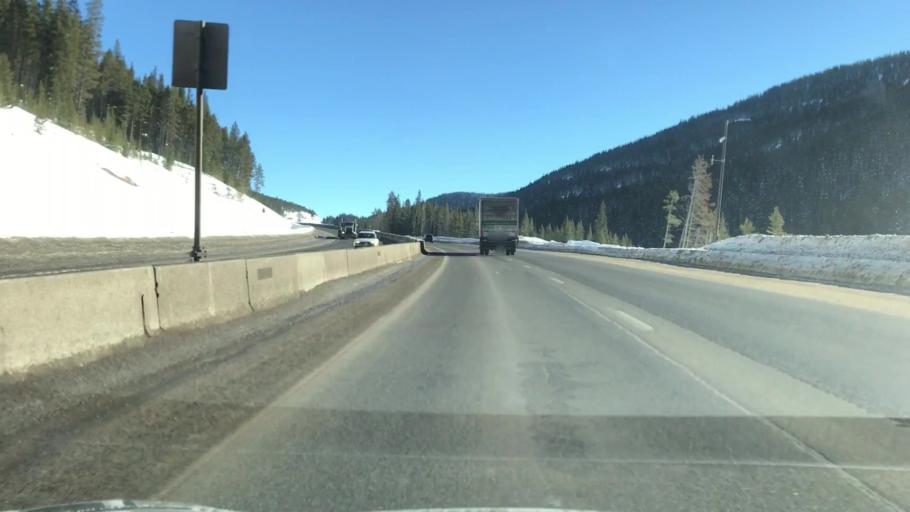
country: US
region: Colorado
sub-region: Eagle County
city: Vail
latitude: 39.5766
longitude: -106.2487
